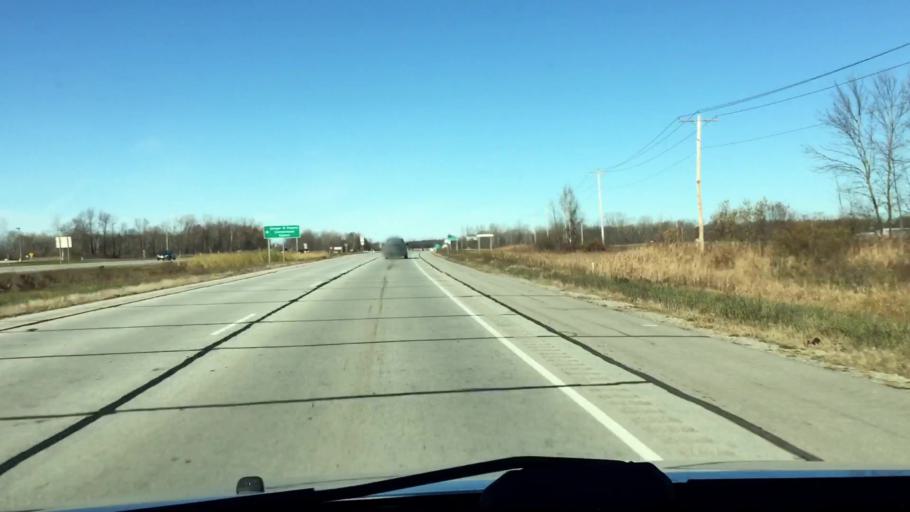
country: US
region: Wisconsin
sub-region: Brown County
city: Oneida
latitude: 44.5827
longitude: -88.1867
